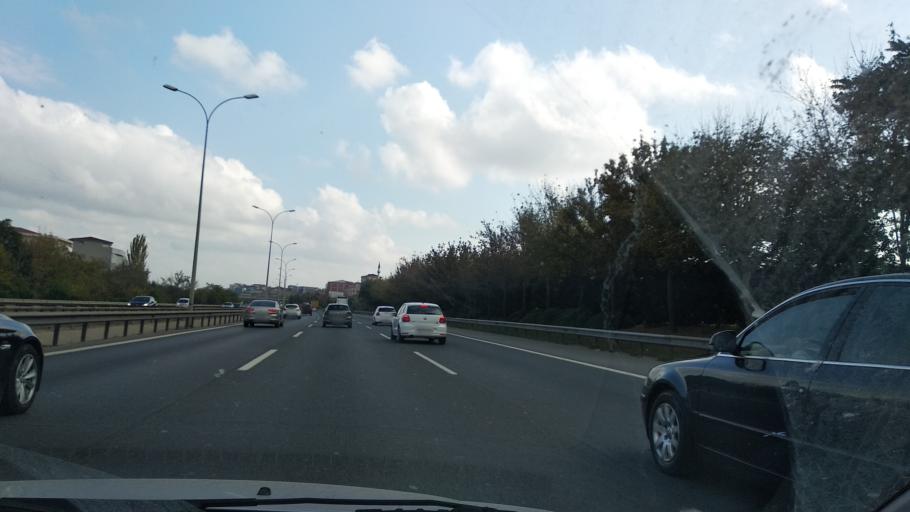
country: TR
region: Istanbul
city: Sultanbeyli
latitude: 40.9652
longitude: 29.2743
